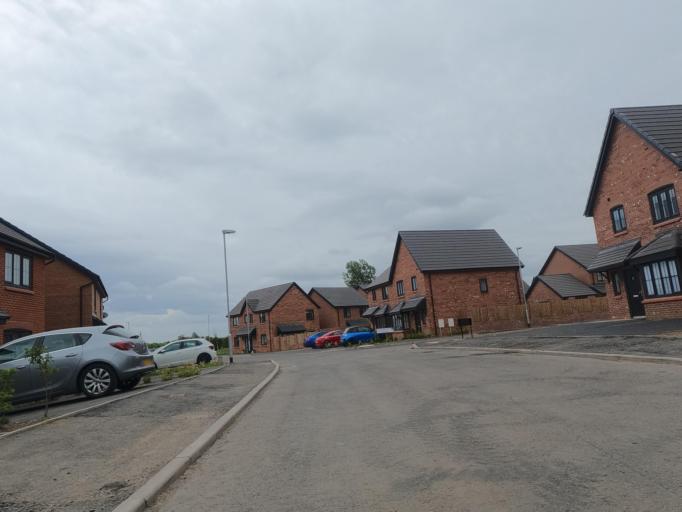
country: GB
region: England
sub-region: Northumberland
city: Blyth
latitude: 55.1116
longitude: -1.5389
